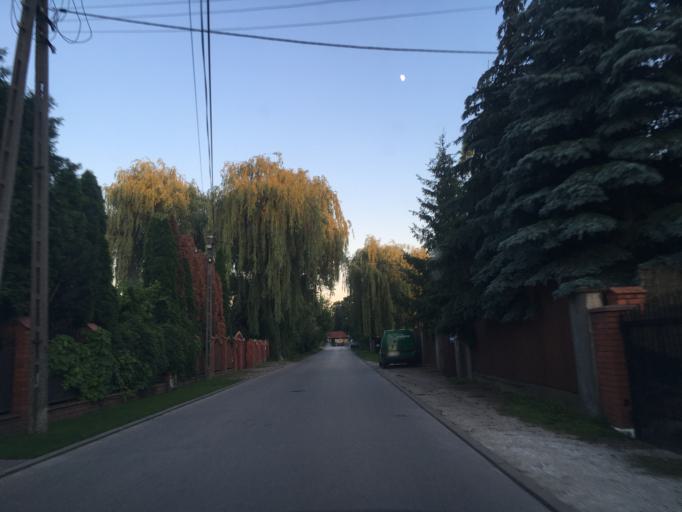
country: PL
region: Masovian Voivodeship
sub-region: Powiat piaseczynski
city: Piaseczno
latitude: 52.0664
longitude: 21.0114
